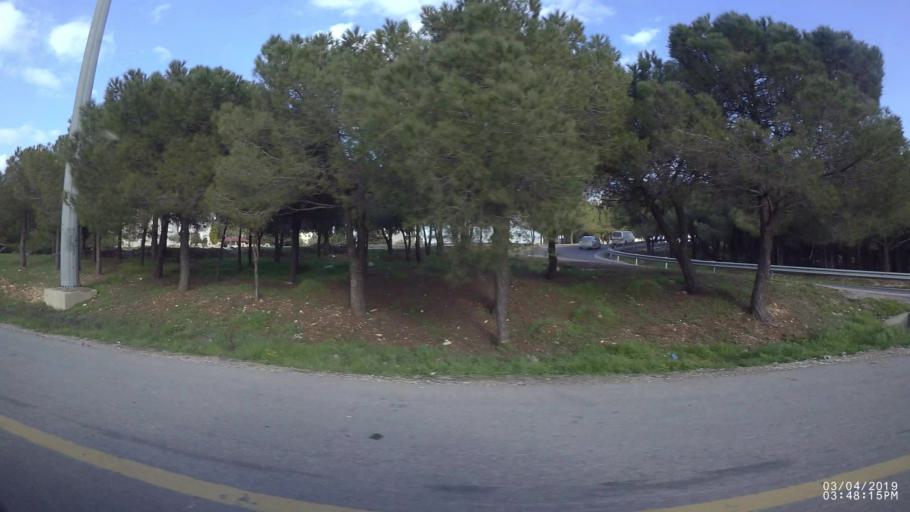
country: JO
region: Amman
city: Umm as Summaq
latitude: 31.9014
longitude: 35.8697
